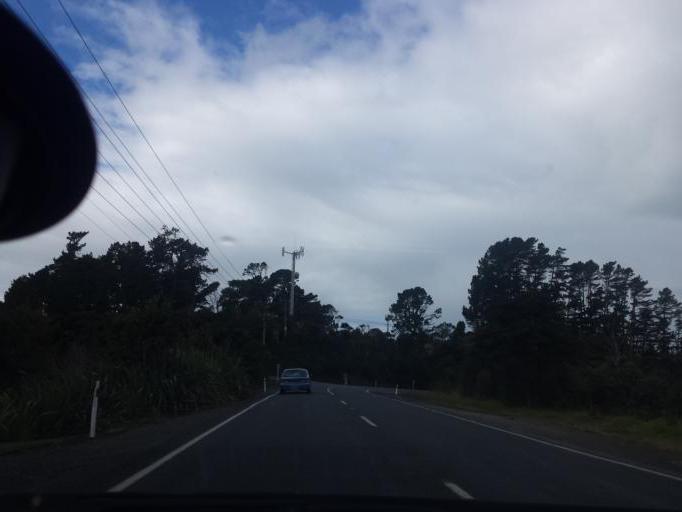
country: NZ
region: Auckland
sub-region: Auckland
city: Warkworth
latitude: -36.4042
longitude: 174.7155
